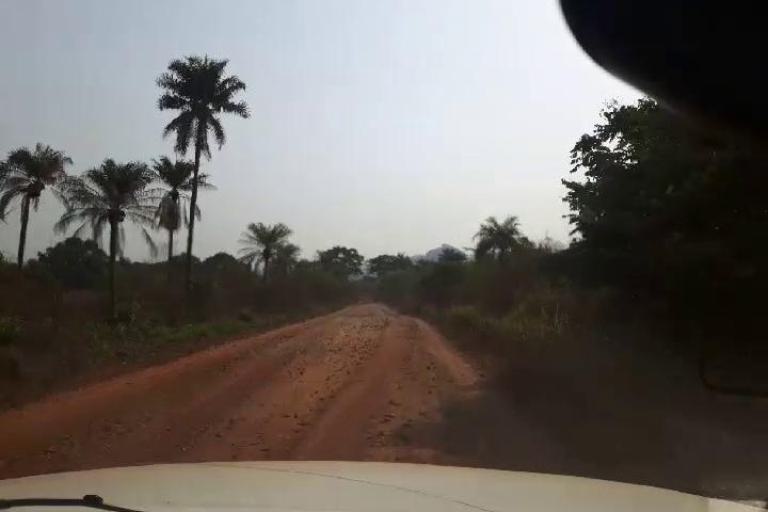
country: SL
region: Northern Province
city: Masingbi
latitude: 8.8476
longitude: -11.8297
